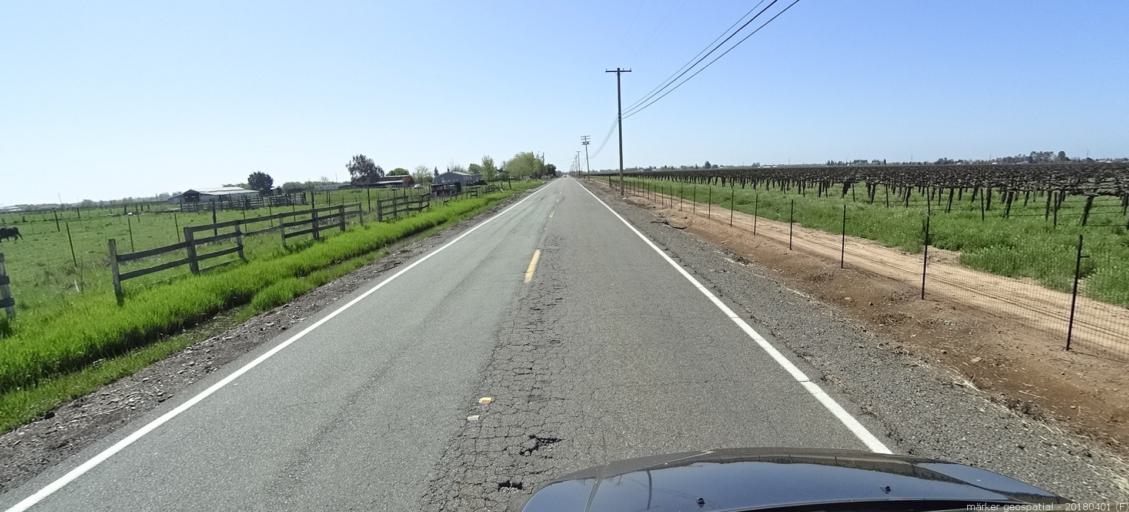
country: US
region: California
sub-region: Sacramento County
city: Herald
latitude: 38.3365
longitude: -121.2238
